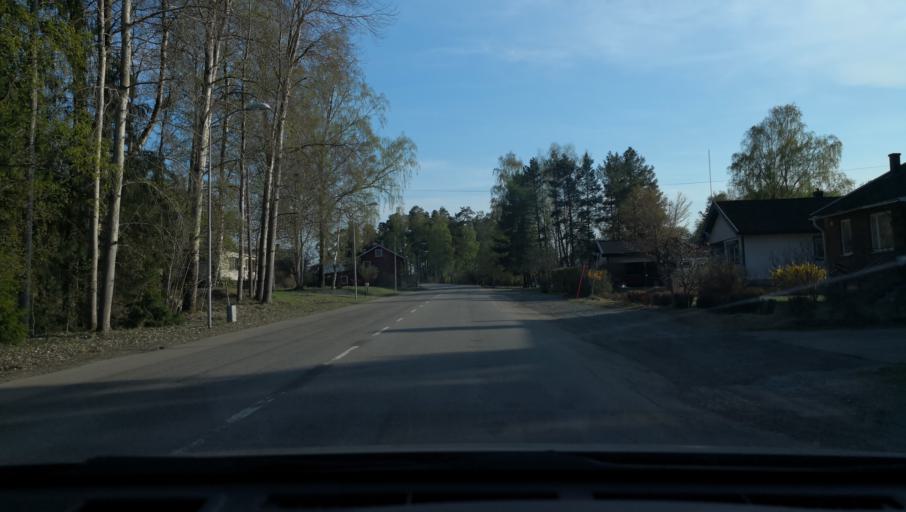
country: SE
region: Uppsala
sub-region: Heby Kommun
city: Tarnsjo
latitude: 60.1662
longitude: 16.9385
